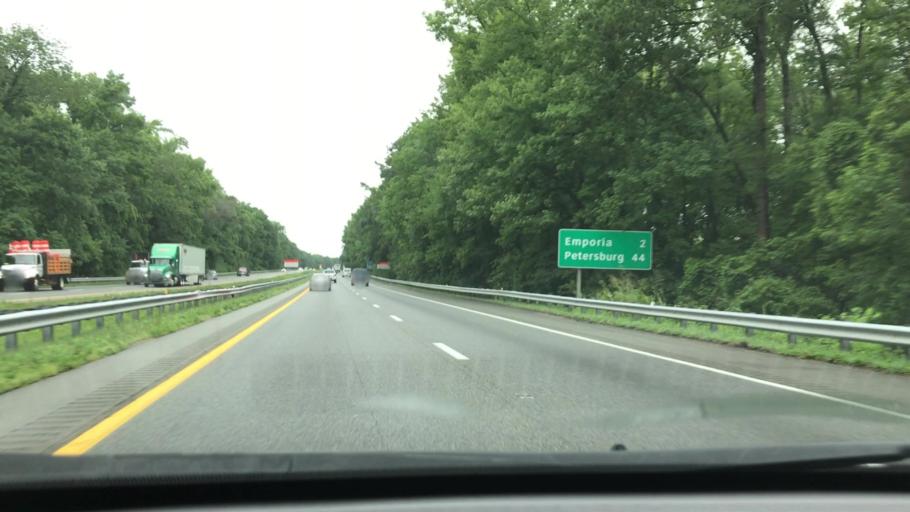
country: US
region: Virginia
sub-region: City of Emporia
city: Emporia
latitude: 36.6752
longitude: -77.5566
